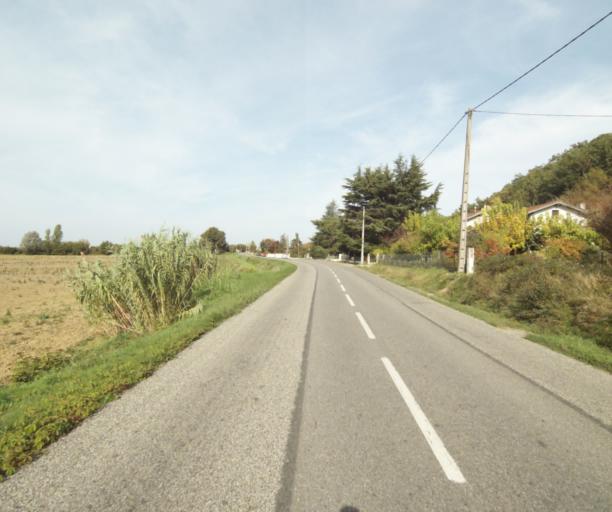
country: FR
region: Midi-Pyrenees
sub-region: Departement du Tarn-et-Garonne
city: Corbarieu
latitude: 43.9535
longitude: 1.3650
